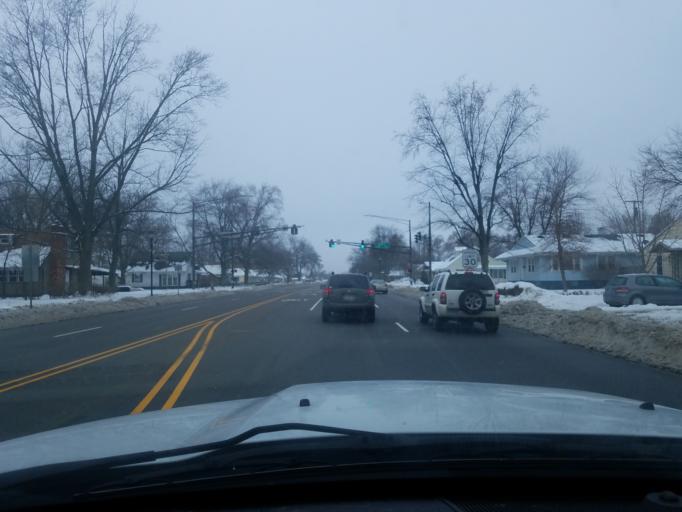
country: US
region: Indiana
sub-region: Saint Joseph County
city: Mishawaka
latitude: 41.6835
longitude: -86.1814
